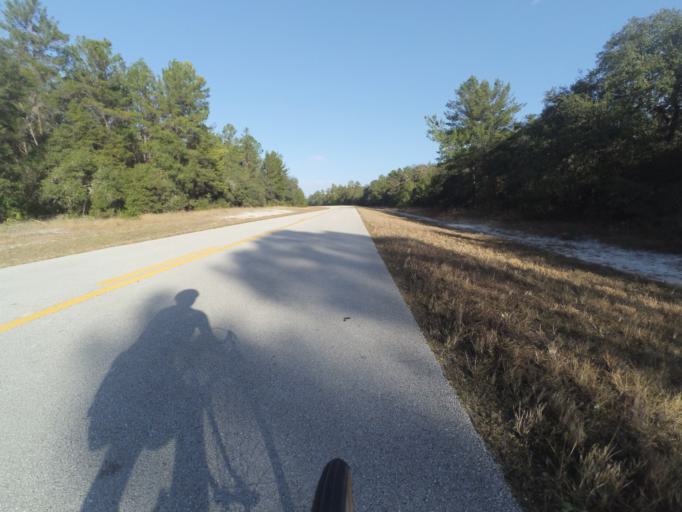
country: US
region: Florida
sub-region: Lake County
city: Astor
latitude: 29.0999
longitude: -81.5652
